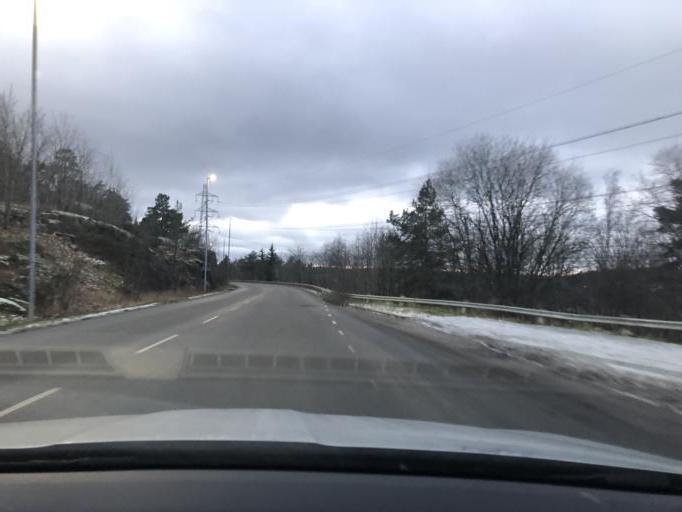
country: SE
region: Stockholm
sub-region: Botkyrka Kommun
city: Fittja
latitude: 59.2425
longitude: 17.8538
